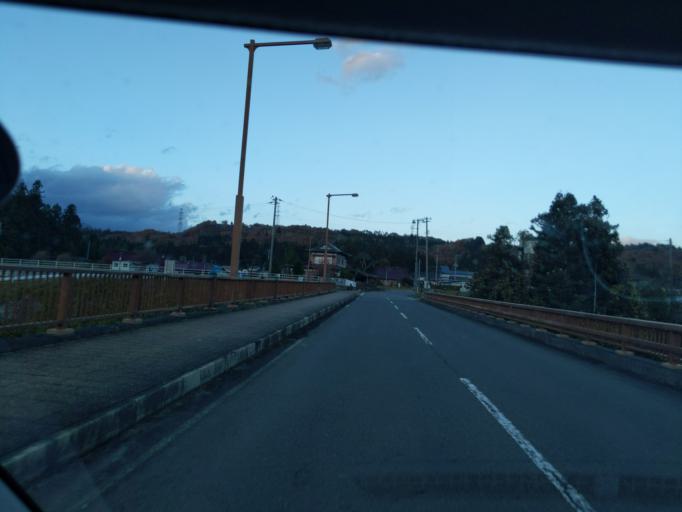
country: JP
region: Iwate
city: Ichinoseki
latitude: 39.0171
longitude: 141.0904
